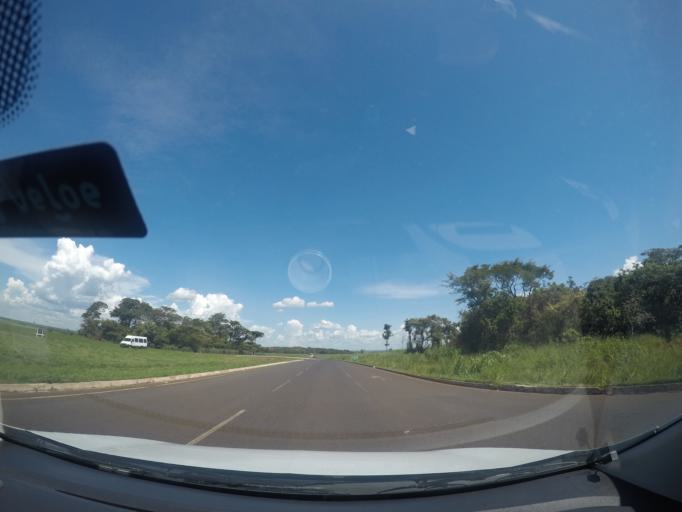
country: BR
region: Minas Gerais
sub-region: Frutal
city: Frutal
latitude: -20.1119
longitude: -48.7010
